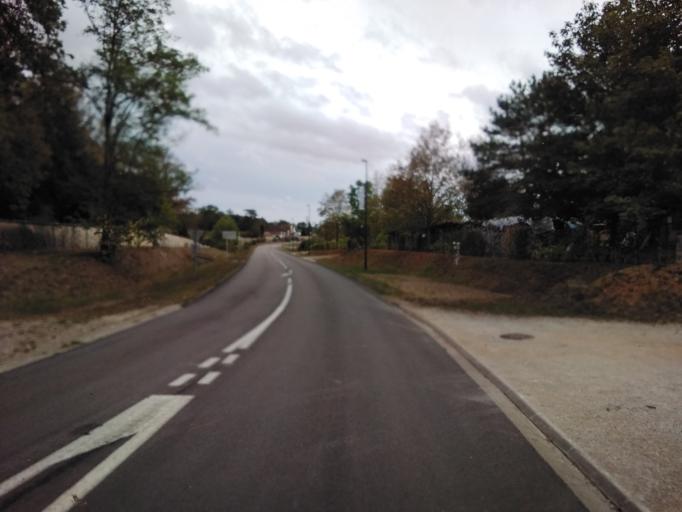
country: FR
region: Champagne-Ardenne
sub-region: Departement de l'Aube
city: Les Riceys
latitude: 47.9892
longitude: 4.3586
